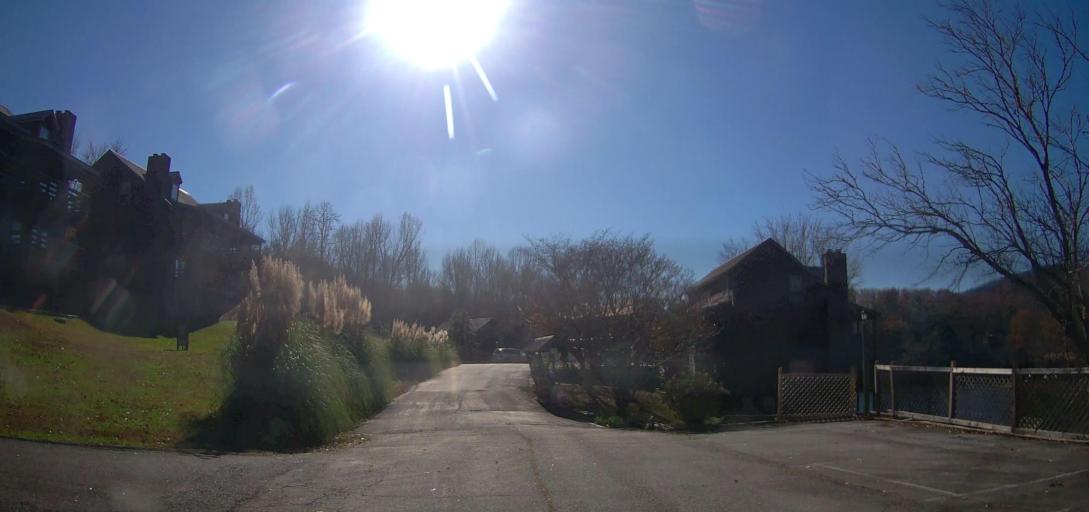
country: US
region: Georgia
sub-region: White County
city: Cleveland
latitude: 34.6512
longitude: -83.7984
